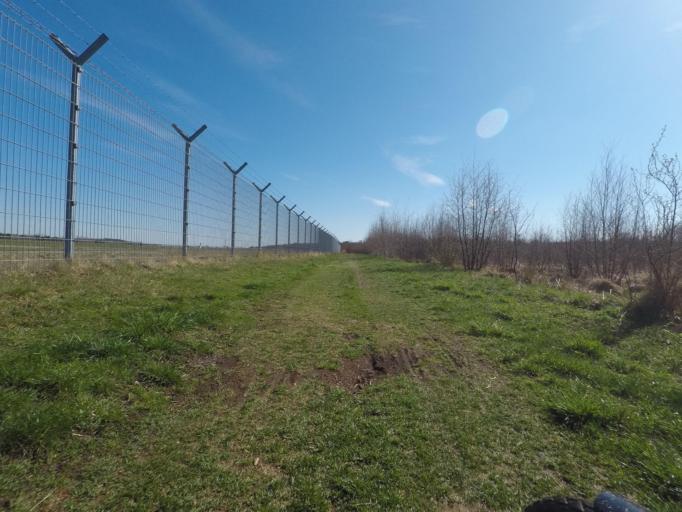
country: DE
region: Hamburg
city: Langenhorn
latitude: 53.6558
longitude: 9.9716
